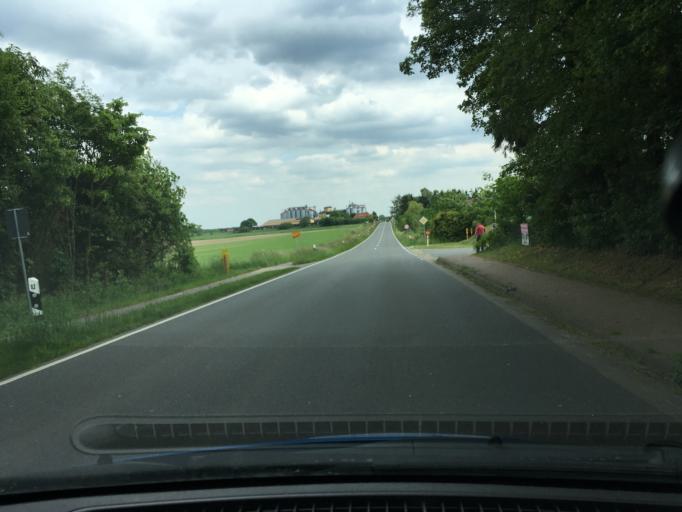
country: DE
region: Lower Saxony
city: Betzendorf
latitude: 53.1505
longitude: 10.2968
